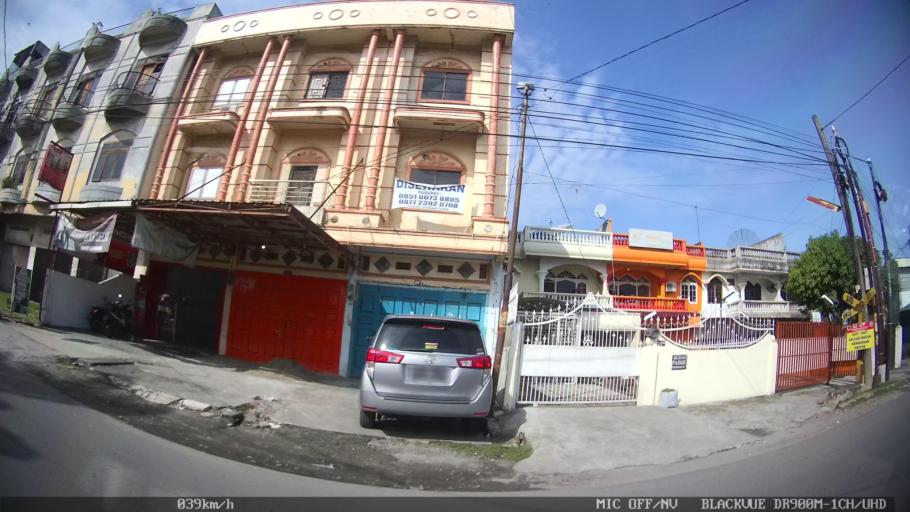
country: ID
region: North Sumatra
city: Medan
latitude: 3.6011
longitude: 98.6617
